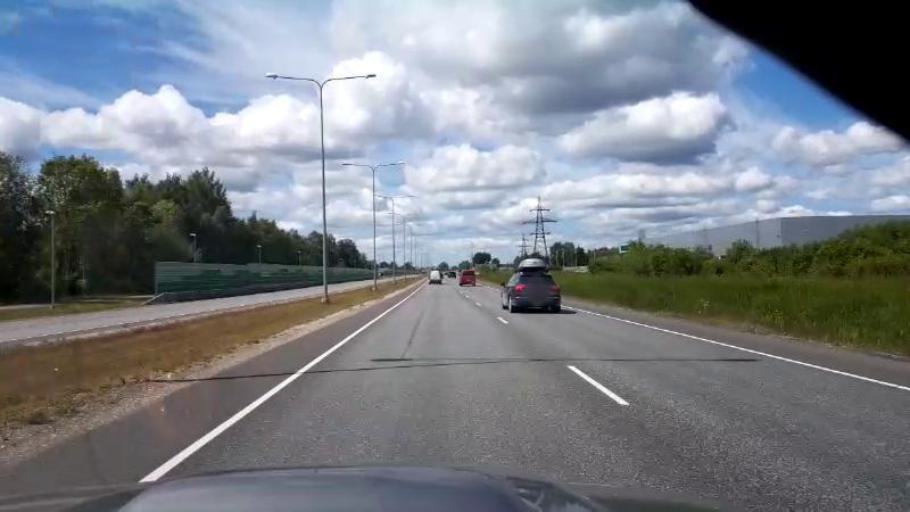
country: EE
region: Paernumaa
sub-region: Paernu linn
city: Parnu
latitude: 58.3964
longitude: 24.5254
